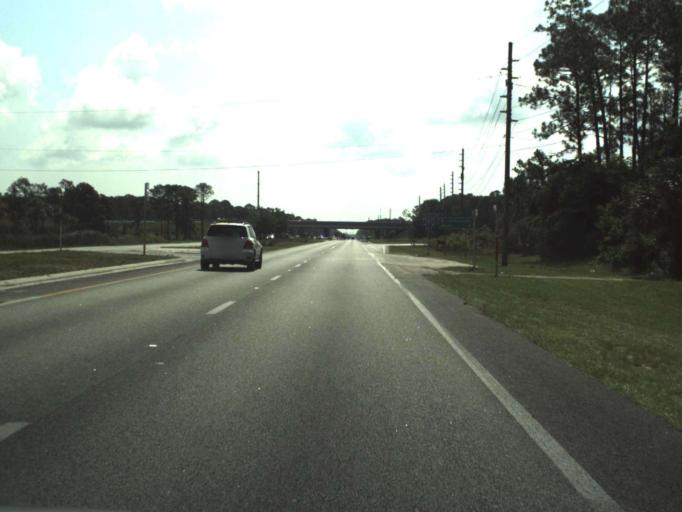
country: US
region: Florida
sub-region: Volusia County
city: Glencoe
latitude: 29.0126
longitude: -80.9924
